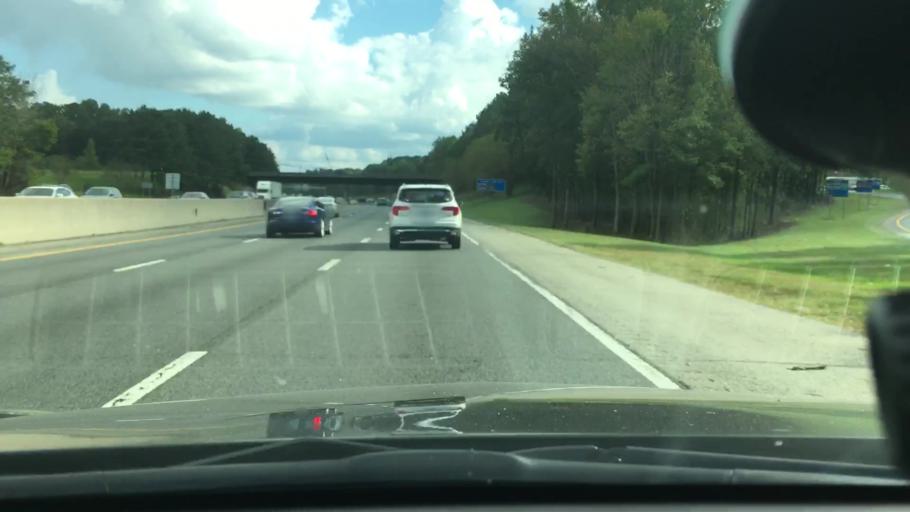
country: US
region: North Carolina
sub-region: Orange County
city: Chapel Hill
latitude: 35.9150
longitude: -78.9835
